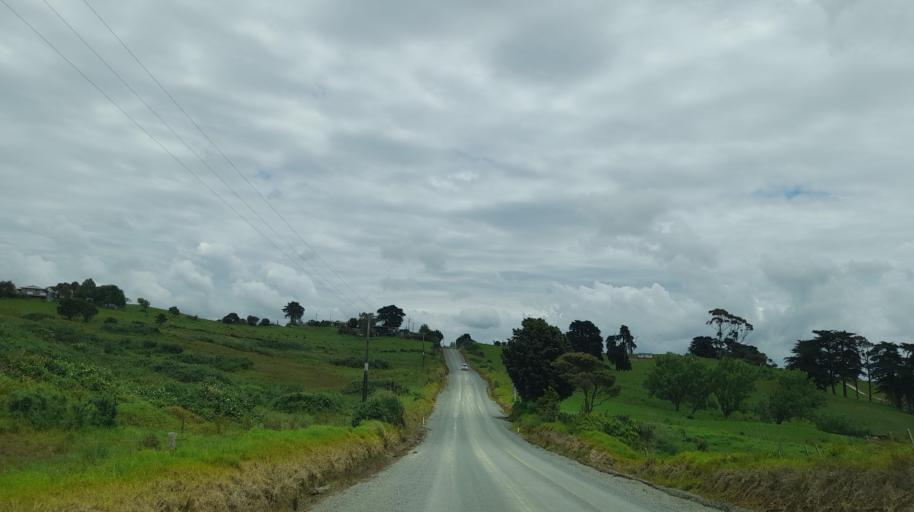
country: NZ
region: Auckland
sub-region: Auckland
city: Wellsford
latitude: -36.2612
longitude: 174.4135
